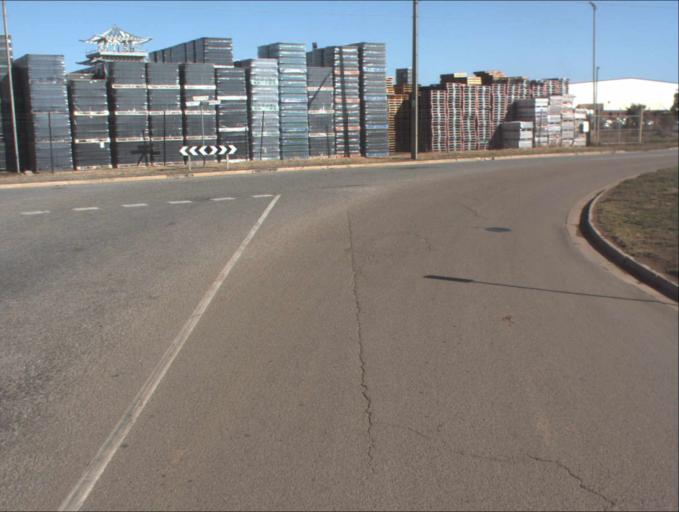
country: AU
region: South Australia
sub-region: Port Adelaide Enfield
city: Alberton
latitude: -34.8416
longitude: 138.5396
